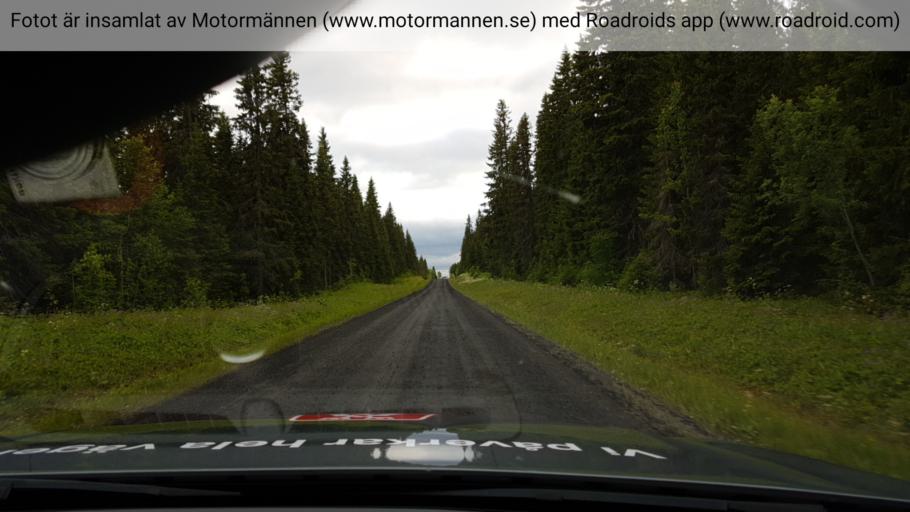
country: SE
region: Jaemtland
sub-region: OEstersunds Kommun
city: Lit
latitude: 63.6208
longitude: 15.0152
